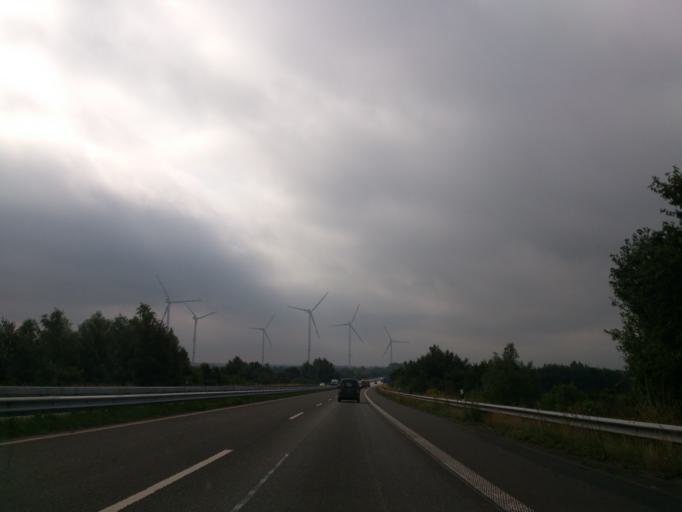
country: DE
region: Schleswig-Holstein
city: Arkebek
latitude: 54.1486
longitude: 9.2410
